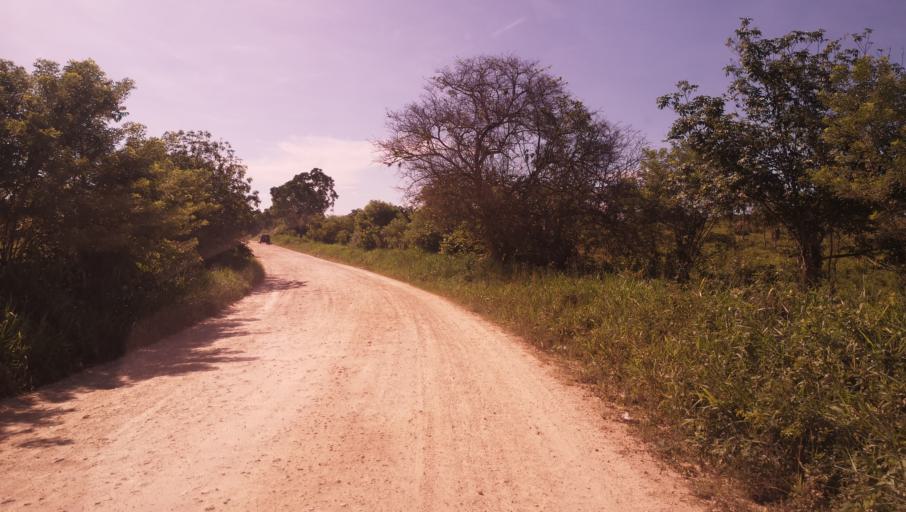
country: GT
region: Peten
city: Dolores
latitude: 16.7211
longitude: -89.3764
